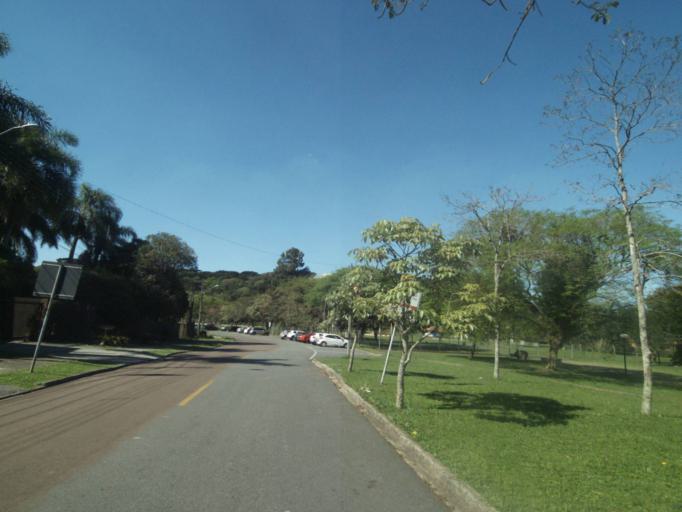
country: BR
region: Parana
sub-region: Curitiba
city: Curitiba
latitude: -25.3908
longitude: -49.2325
